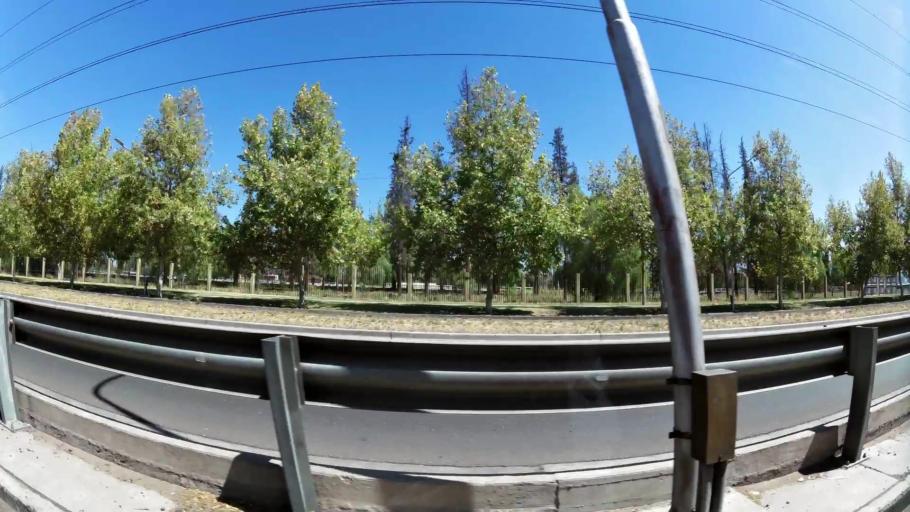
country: AR
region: Mendoza
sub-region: Departamento de Godoy Cruz
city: Godoy Cruz
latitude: -32.9111
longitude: -68.8641
